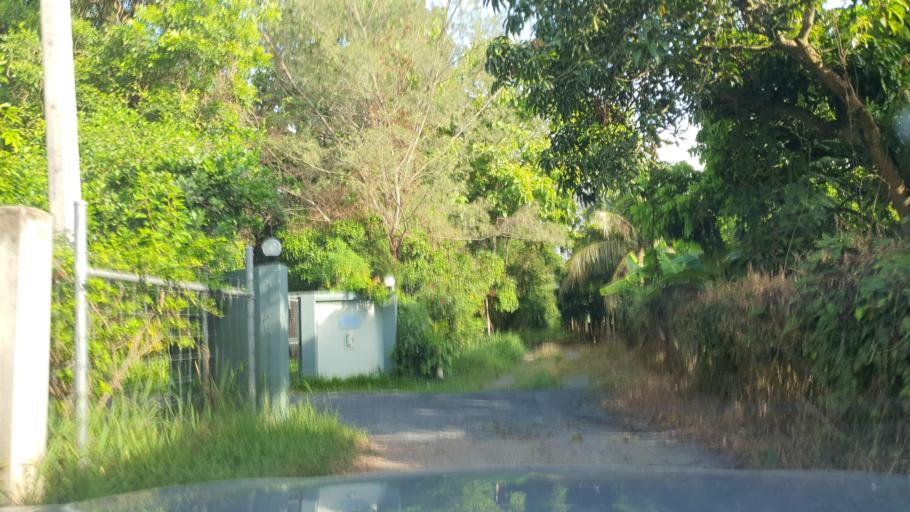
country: TH
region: Chiang Mai
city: San Kamphaeng
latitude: 18.7473
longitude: 99.1001
